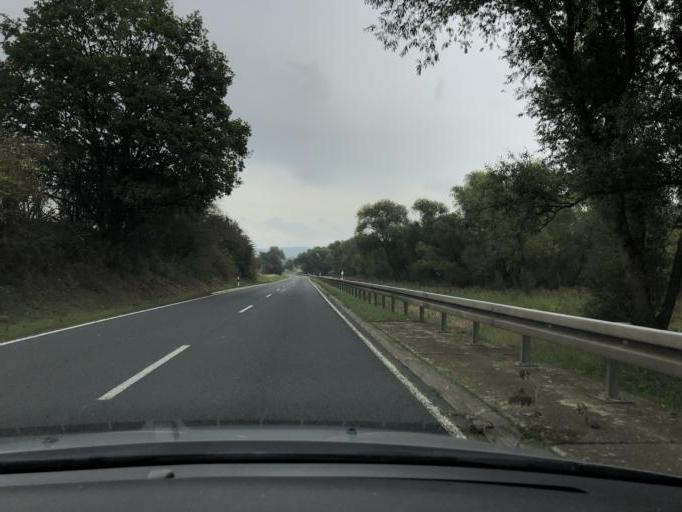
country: DE
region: Thuringia
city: Auleben
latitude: 51.3984
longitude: 10.9457
